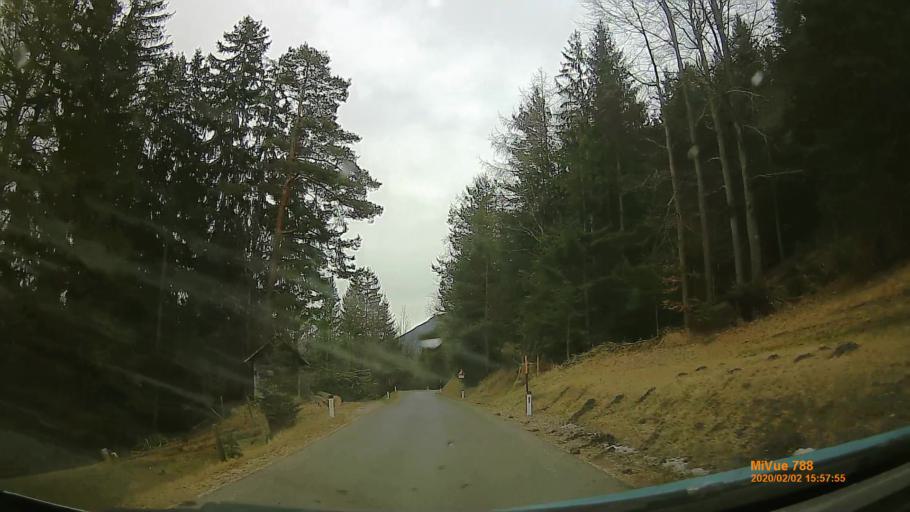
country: AT
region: Lower Austria
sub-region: Politischer Bezirk Neunkirchen
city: Semmering
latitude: 47.6612
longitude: 15.7942
